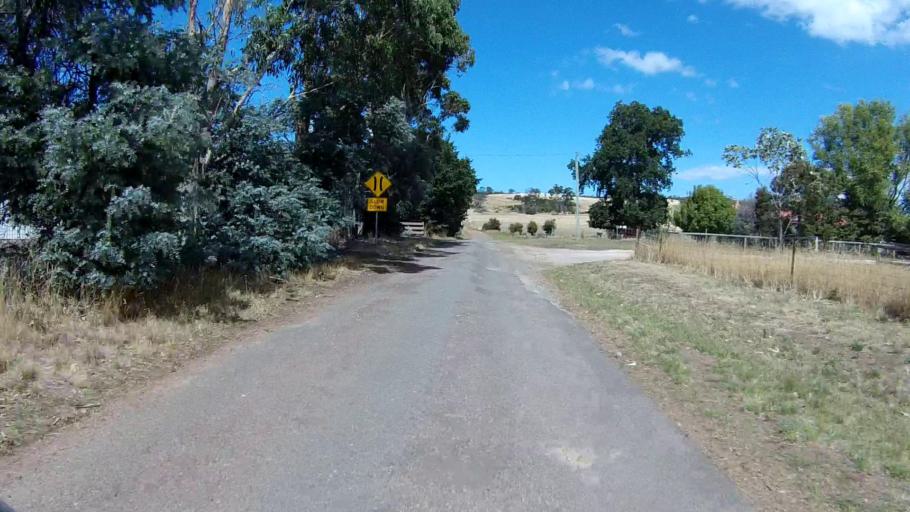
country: AU
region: Tasmania
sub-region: Break O'Day
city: St Helens
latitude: -41.9620
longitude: 148.0714
